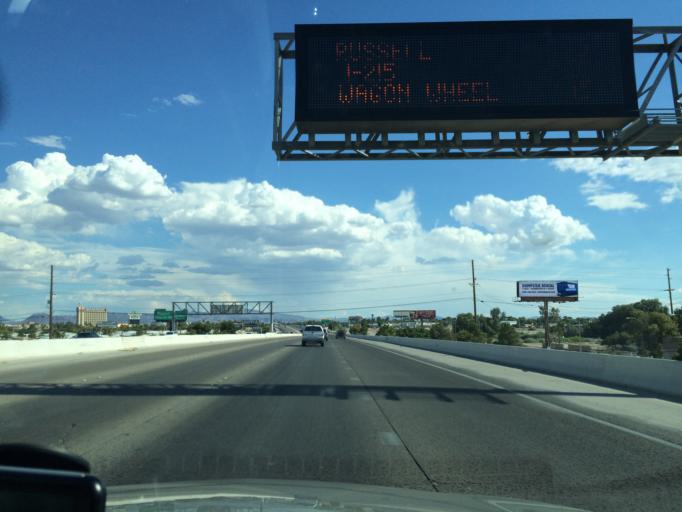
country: US
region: Nevada
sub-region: Clark County
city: Winchester
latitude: 36.1461
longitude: -115.0915
